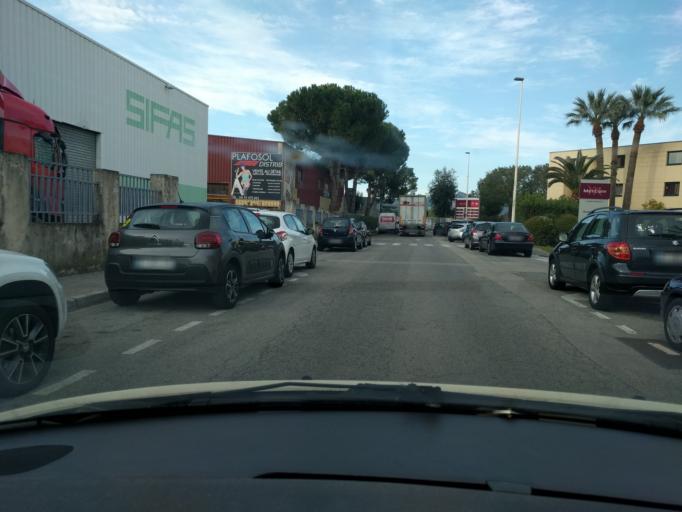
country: FR
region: Provence-Alpes-Cote d'Azur
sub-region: Departement des Alpes-Maritimes
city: Mandelieu-la-Napoule
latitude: 43.5428
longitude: 6.9562
